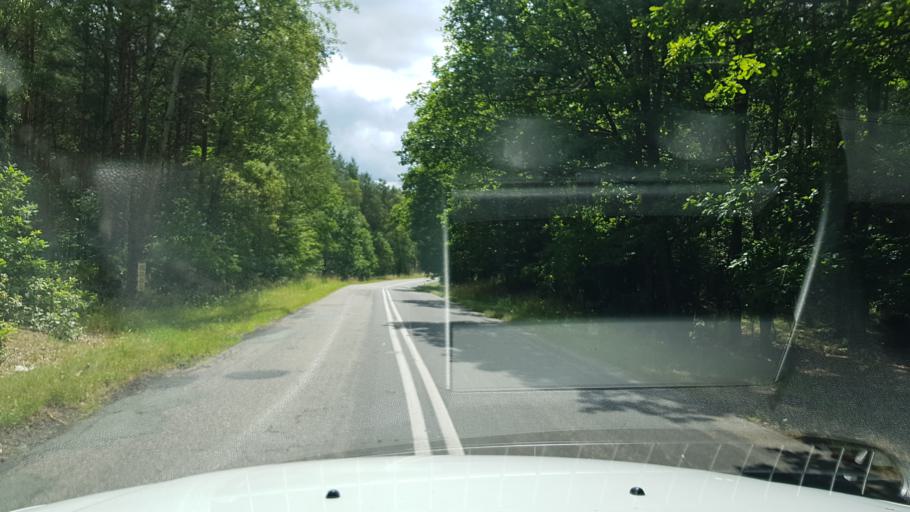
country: PL
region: West Pomeranian Voivodeship
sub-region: Powiat stargardzki
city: Insko
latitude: 53.3642
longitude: 15.5874
